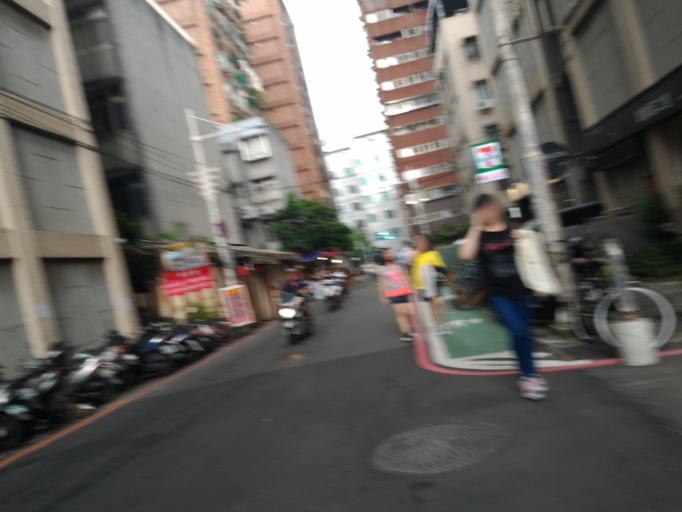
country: TW
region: Taipei
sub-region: Taipei
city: Banqiao
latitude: 25.0021
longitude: 121.5119
